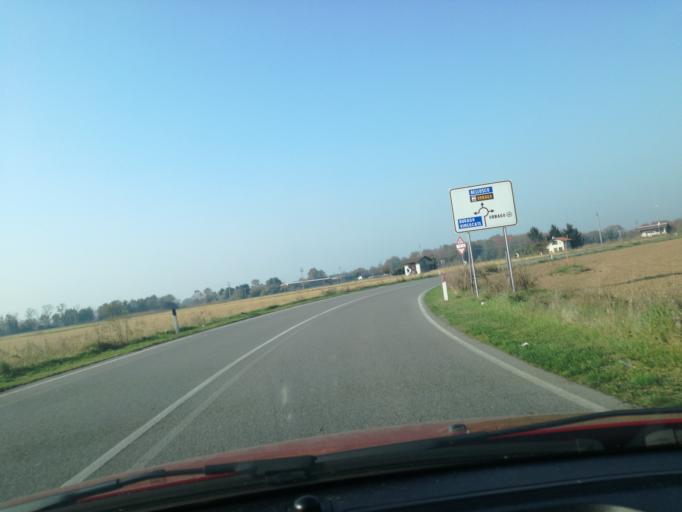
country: IT
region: Lombardy
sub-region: Provincia di Monza e Brianza
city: Cavenago di Brianza
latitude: 45.5935
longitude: 9.4103
